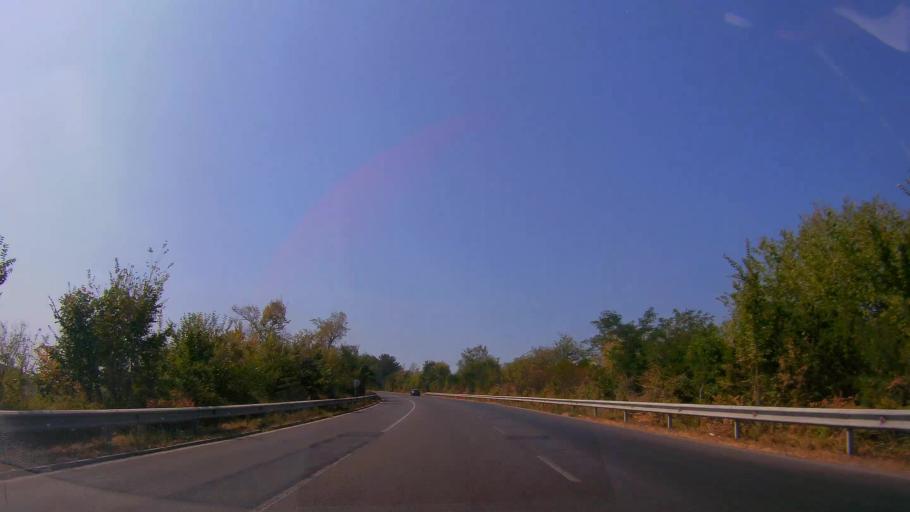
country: BG
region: Ruse
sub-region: Obshtina Vetovo
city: Senovo
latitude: 43.5613
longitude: 26.3794
